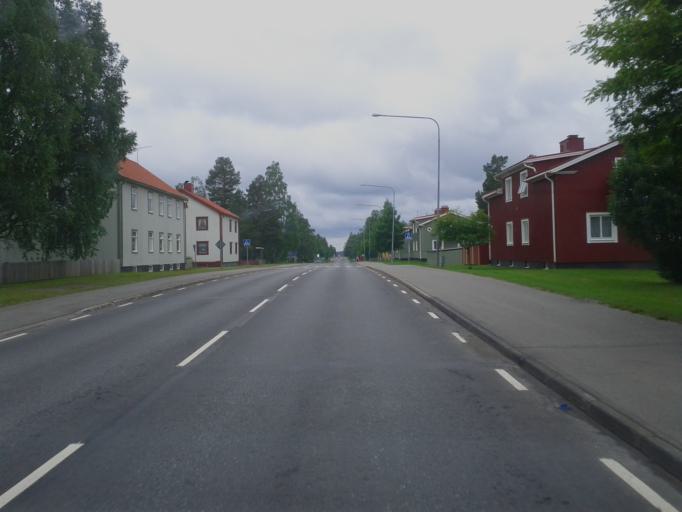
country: SE
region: Vaesterbotten
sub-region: Skelleftea Kommun
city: Boliden
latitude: 64.8659
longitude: 20.3885
